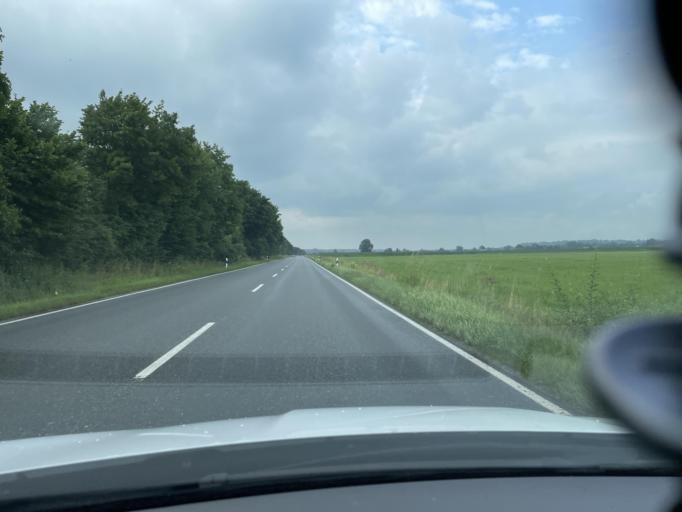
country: DE
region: Bavaria
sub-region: Upper Bavaria
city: Schechen
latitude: 47.9424
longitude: 12.1329
